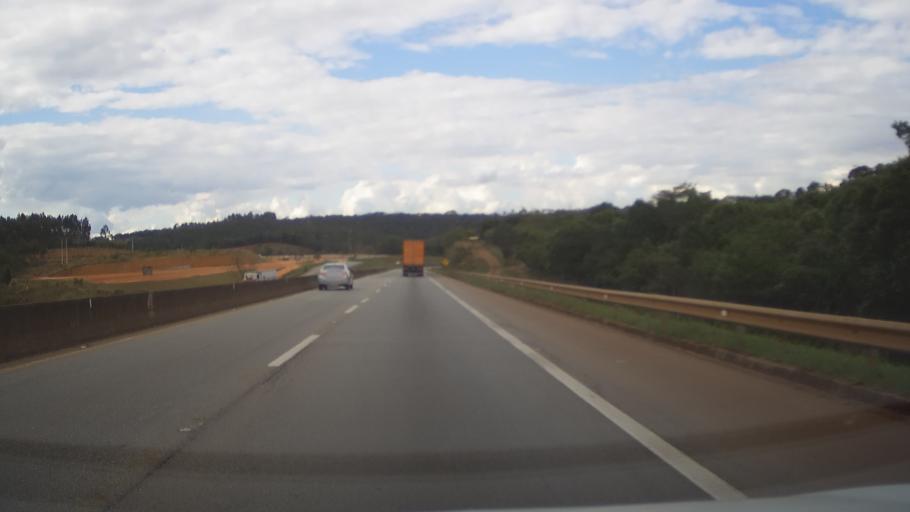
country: BR
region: Minas Gerais
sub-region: Itauna
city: Itauna
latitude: -20.2896
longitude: -44.4360
